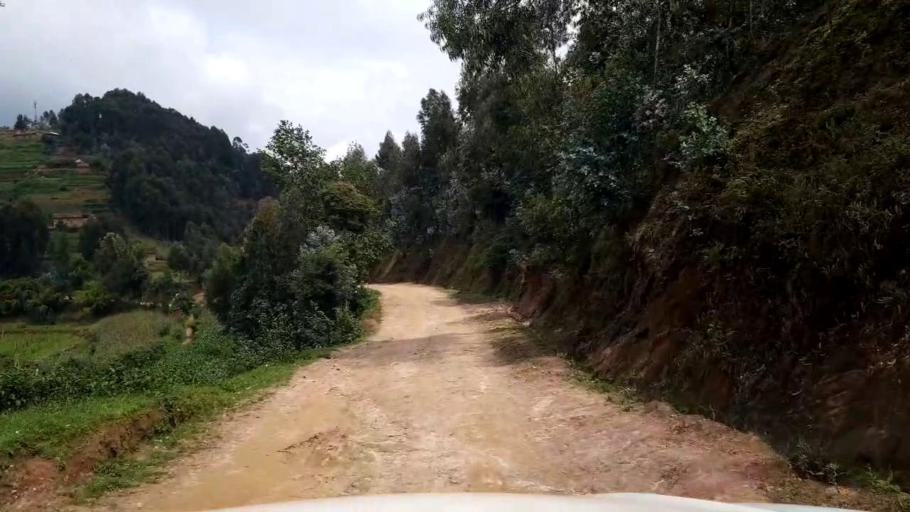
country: RW
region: Western Province
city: Kibuye
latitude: -1.9381
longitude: 29.4460
